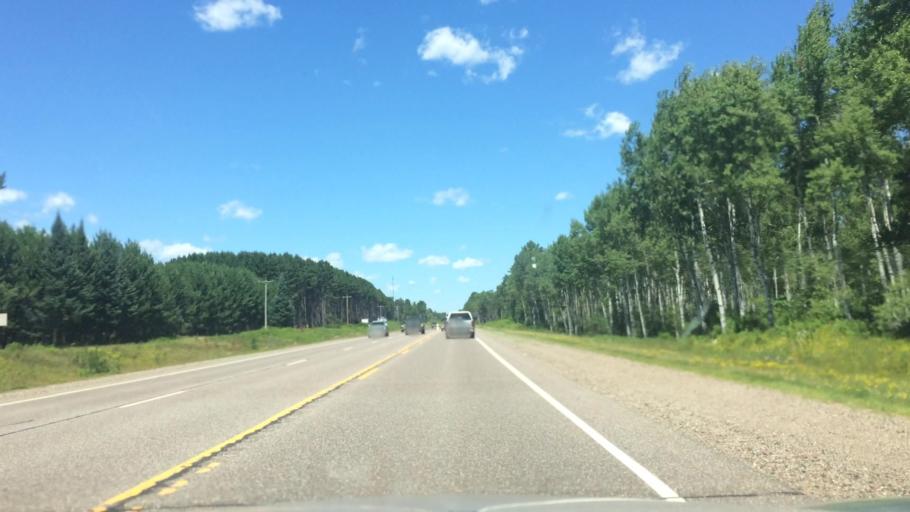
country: US
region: Wisconsin
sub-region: Lincoln County
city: Tomahawk
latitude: 45.6681
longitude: -89.7141
